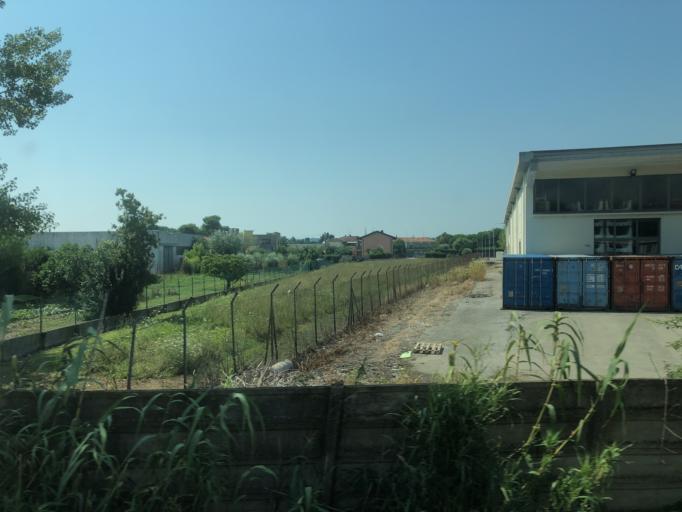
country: IT
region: Emilia-Romagna
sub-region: Provincia di Rimini
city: Rimini
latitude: 44.0708
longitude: 12.5323
